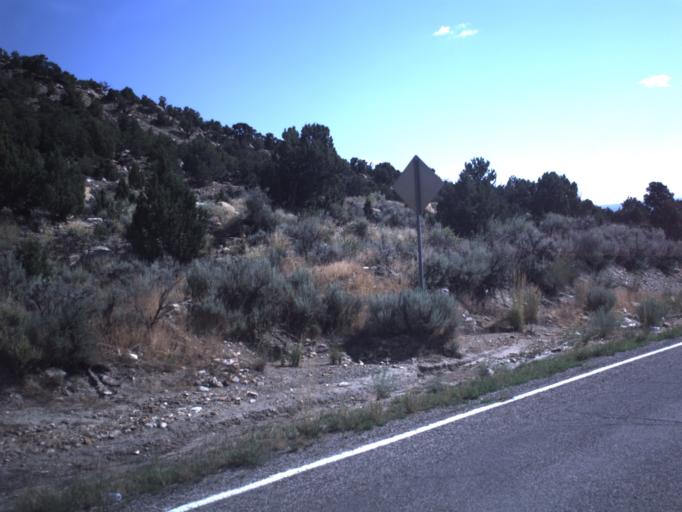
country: US
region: Utah
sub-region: Carbon County
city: Helper
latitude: 39.6797
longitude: -110.8076
